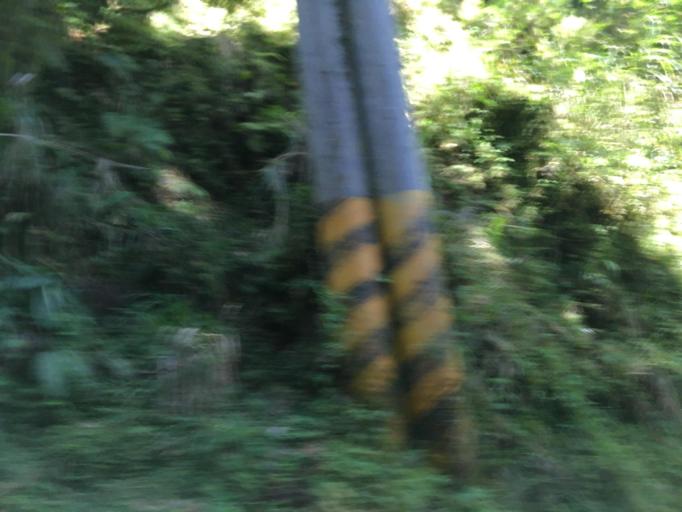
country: TW
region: Taiwan
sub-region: Yilan
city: Yilan
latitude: 24.6181
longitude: 121.4694
